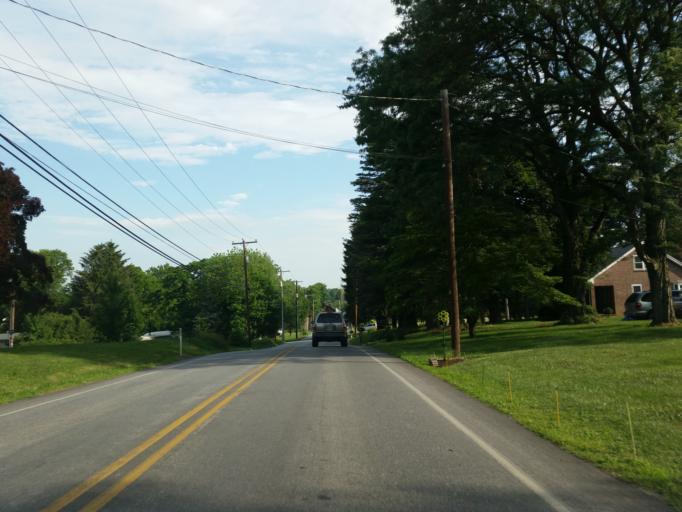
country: US
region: Pennsylvania
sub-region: Lancaster County
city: Lampeter
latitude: 40.0232
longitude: -76.2405
